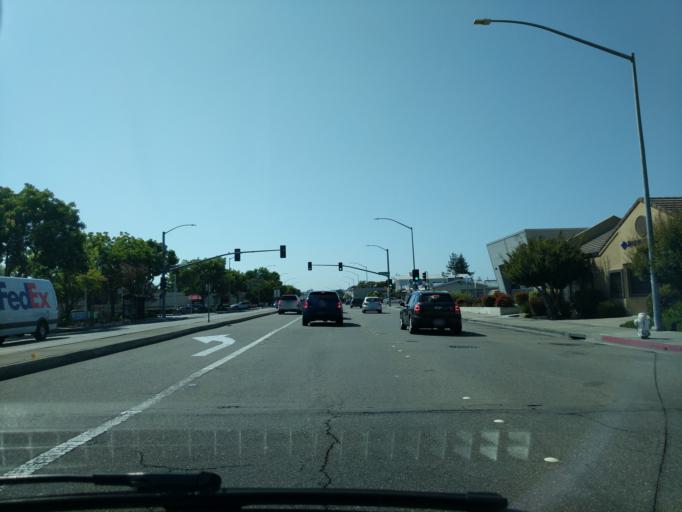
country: US
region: California
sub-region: Alameda County
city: Castro Valley
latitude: 37.6946
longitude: -122.0702
